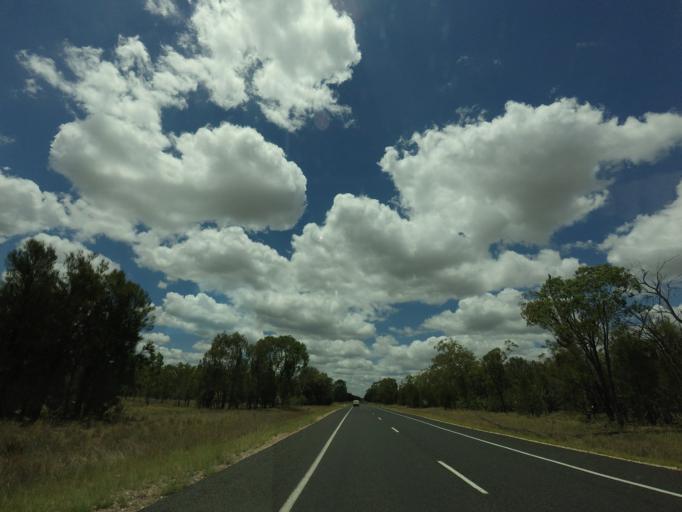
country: AU
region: Queensland
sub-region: Goondiwindi
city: Goondiwindi
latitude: -28.0681
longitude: 150.7550
